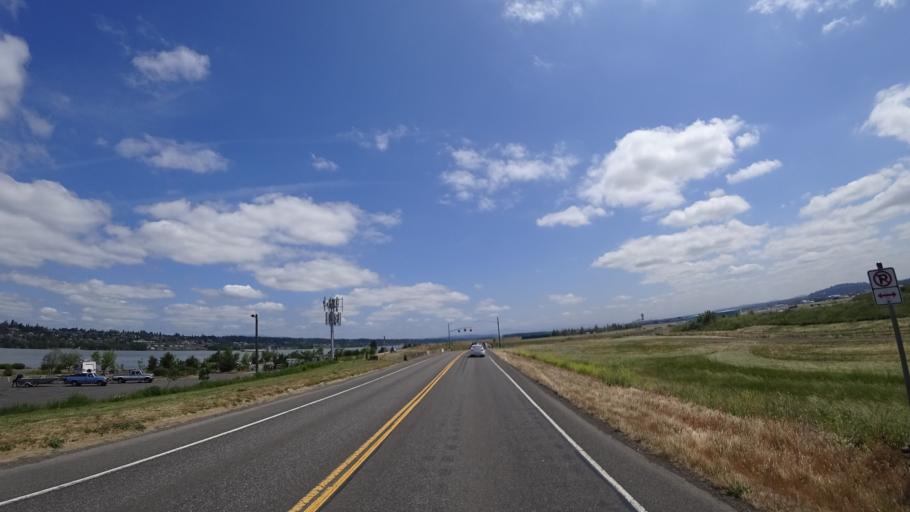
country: US
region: Washington
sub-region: Clark County
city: Vancouver
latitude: 45.5998
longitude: -122.6187
